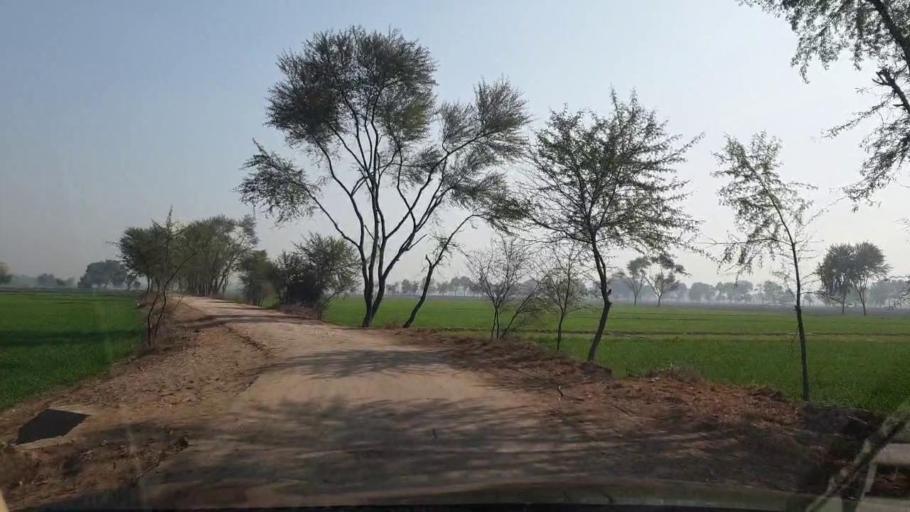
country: PK
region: Sindh
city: Ubauro
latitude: 28.1127
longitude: 69.7445
